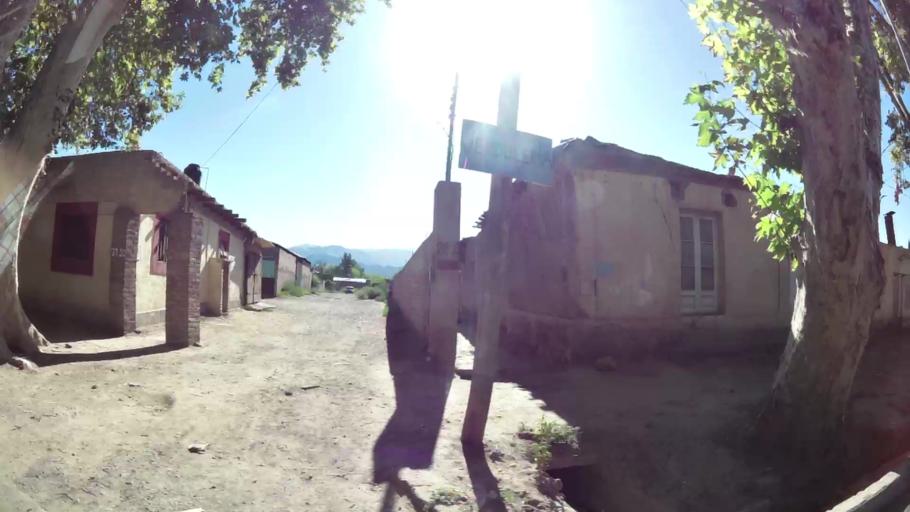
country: AR
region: Mendoza
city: Las Heras
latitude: -32.8387
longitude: -68.8254
